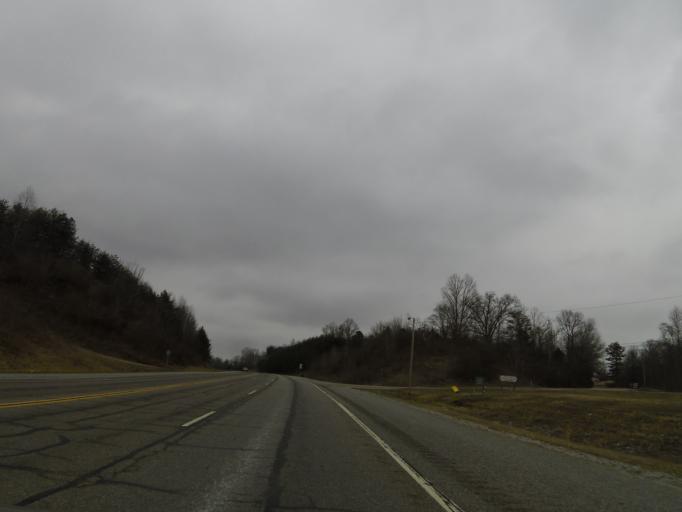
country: US
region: Tennessee
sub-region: Scott County
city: Huntsville
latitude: 36.3881
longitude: -84.5426
